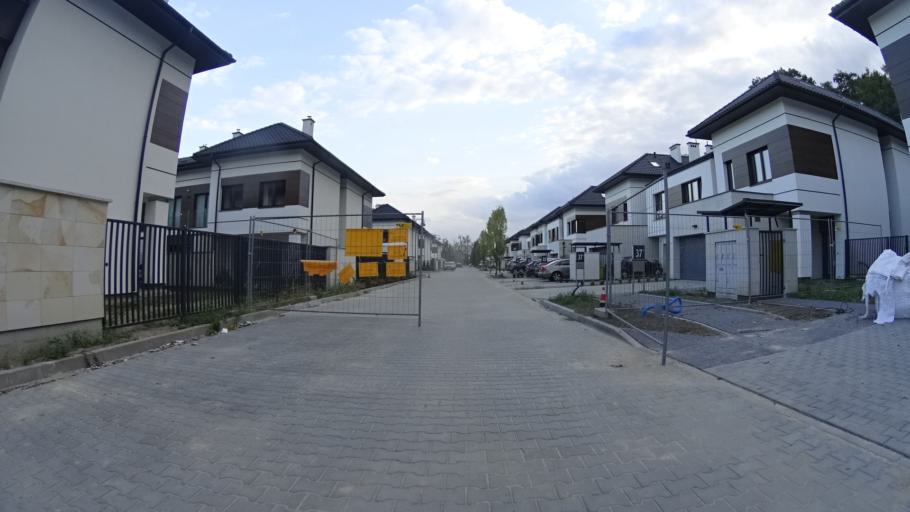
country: PL
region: Masovian Voivodeship
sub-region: Powiat warszawski zachodni
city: Ozarow Mazowiecki
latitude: 52.2336
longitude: 20.8064
